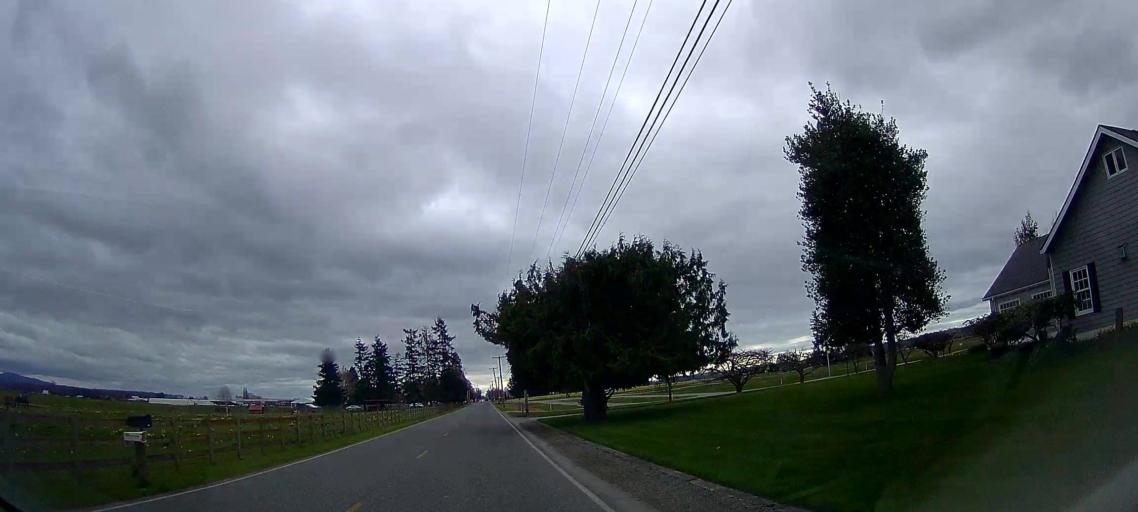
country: US
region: Washington
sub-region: Skagit County
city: Mount Vernon
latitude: 48.4190
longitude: -122.4010
